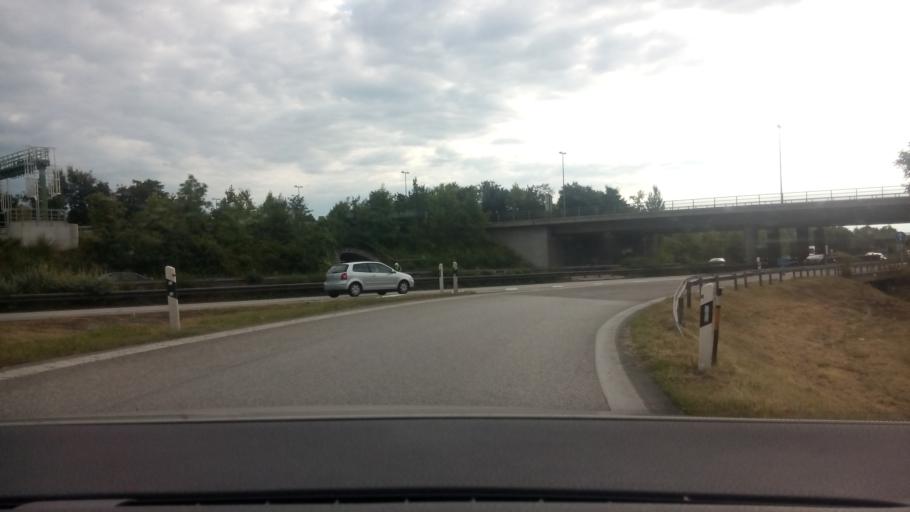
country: DE
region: Bavaria
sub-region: Upper Bavaria
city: Karlsfeld
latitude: 48.2083
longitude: 11.4838
